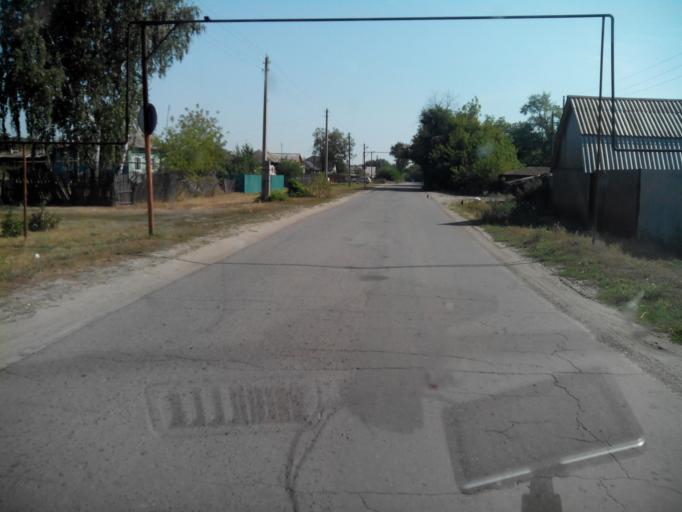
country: RU
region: Samara
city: Balasheyka
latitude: 53.1709
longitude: 48.1345
